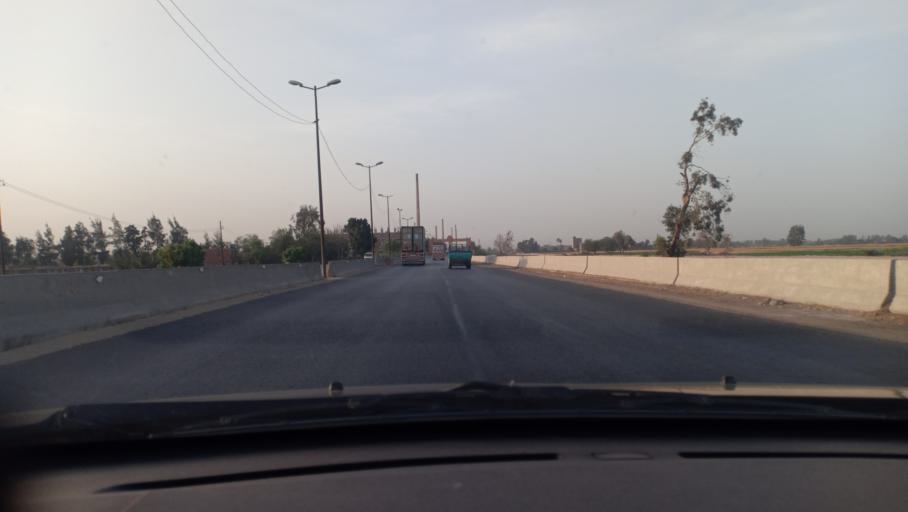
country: EG
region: Muhafazat al Gharbiyah
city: Zifta
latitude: 30.5997
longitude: 31.2744
